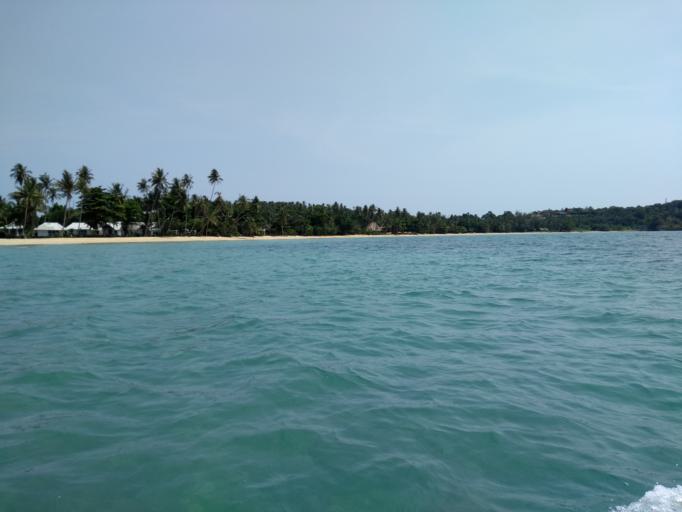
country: TH
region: Trat
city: Ko Kut
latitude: 11.8255
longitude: 102.4687
